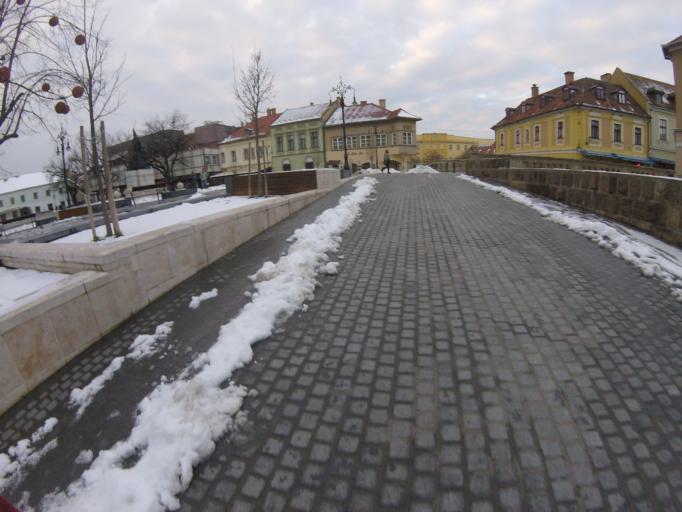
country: HU
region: Heves
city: Eger
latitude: 47.9028
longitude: 20.3777
